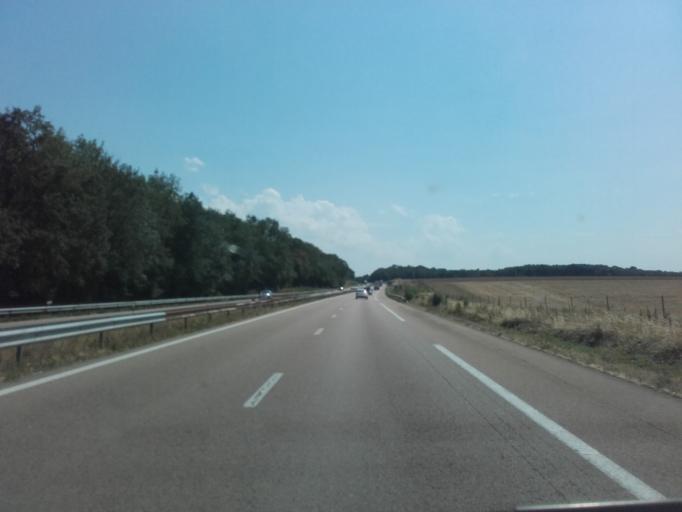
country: FR
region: Bourgogne
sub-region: Departement de l'Yonne
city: Joux-la-Ville
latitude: 47.6122
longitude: 3.9096
